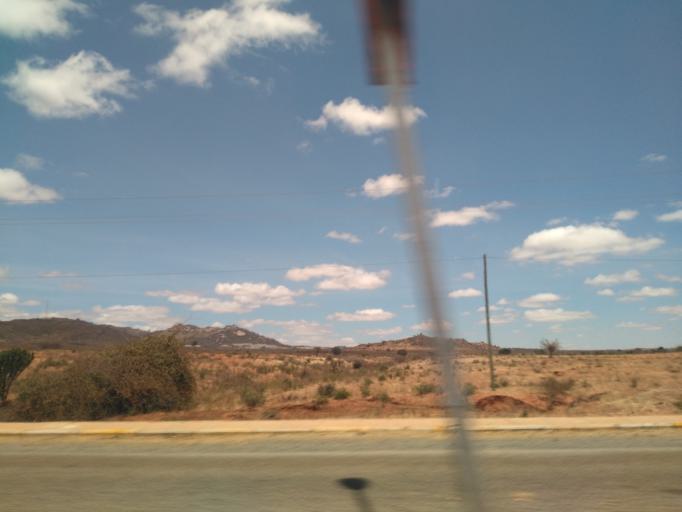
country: TZ
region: Dodoma
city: Kisasa
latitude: -6.2017
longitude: 35.8241
